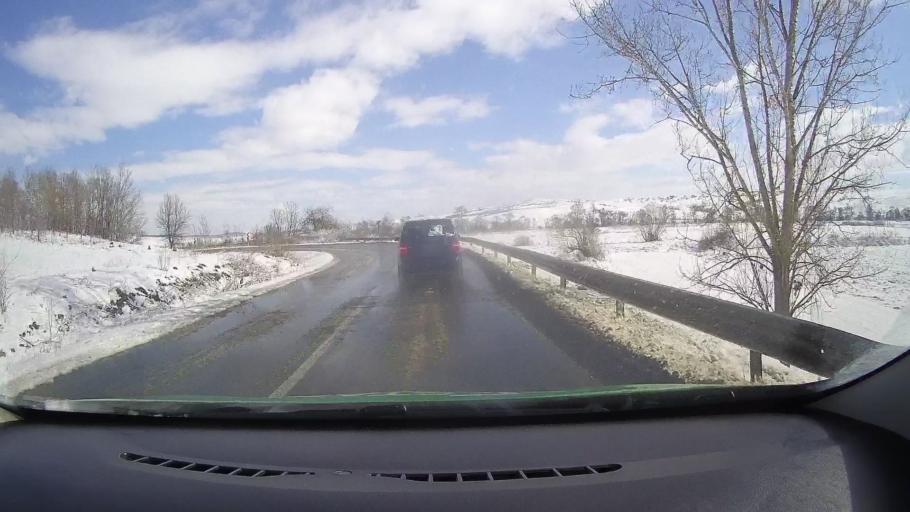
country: RO
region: Sibiu
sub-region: Comuna Nocrich
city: Nocrich
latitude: 45.9021
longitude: 24.4638
